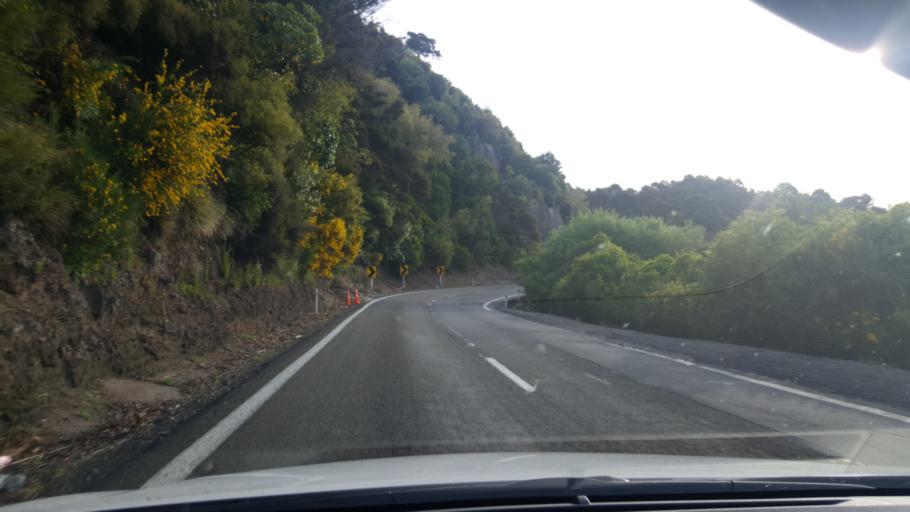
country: NZ
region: Waikato
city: Turangi
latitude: -38.8823
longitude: 175.9700
